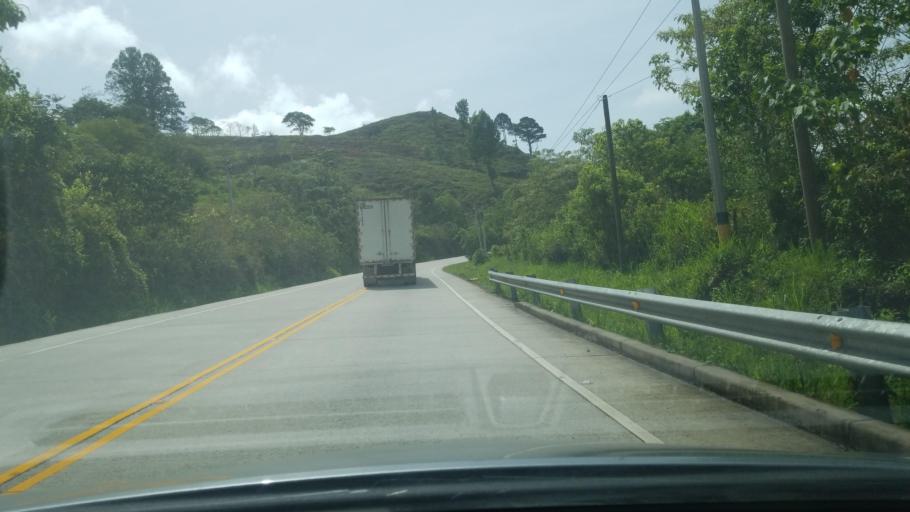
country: HN
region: Copan
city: San Jeronimo
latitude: 14.9309
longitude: -88.9489
